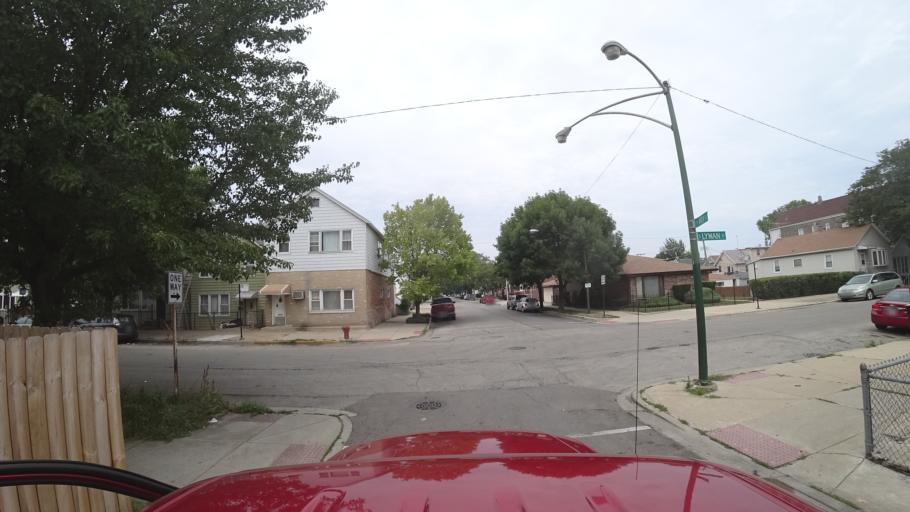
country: US
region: Illinois
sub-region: Cook County
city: Chicago
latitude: 41.8387
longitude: -87.6577
